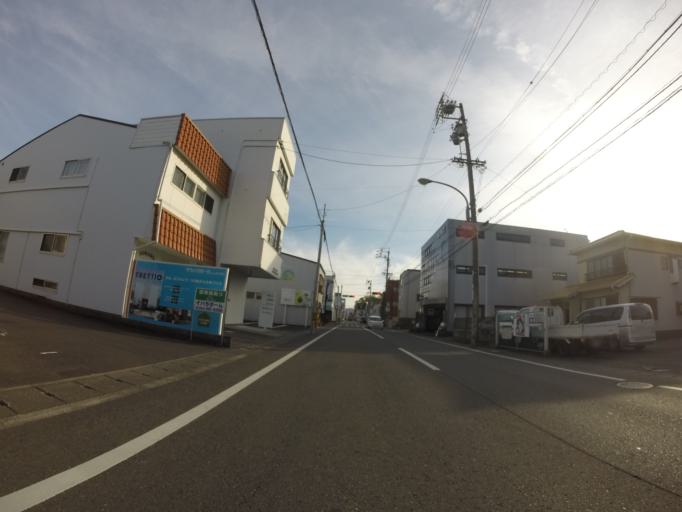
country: JP
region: Shizuoka
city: Shizuoka-shi
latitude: 35.0263
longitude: 138.4820
